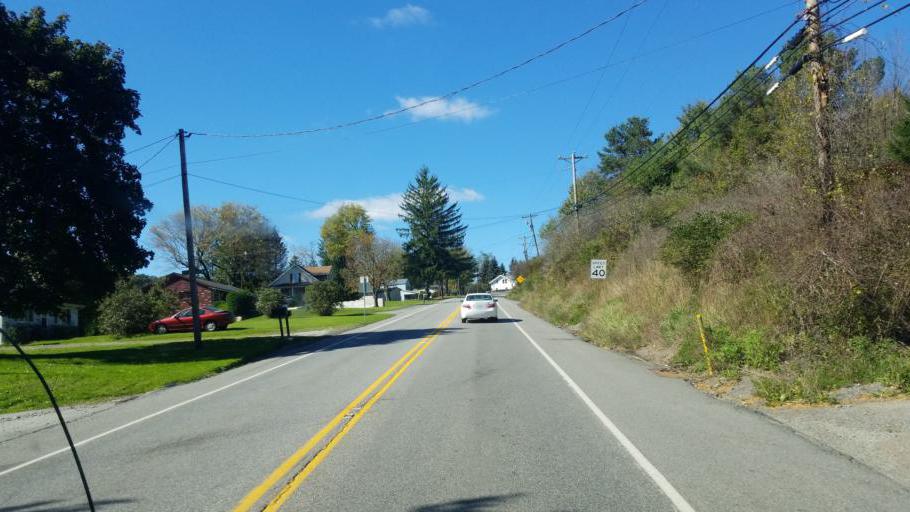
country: US
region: Pennsylvania
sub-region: Somerset County
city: Boswell
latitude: 40.1486
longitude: -79.0455
